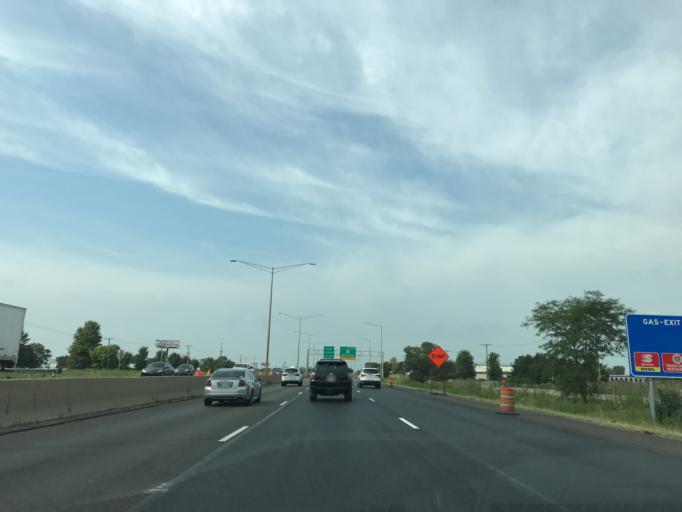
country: US
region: Illinois
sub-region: Will County
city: Bolingbrook
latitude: 41.6918
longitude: -88.0554
